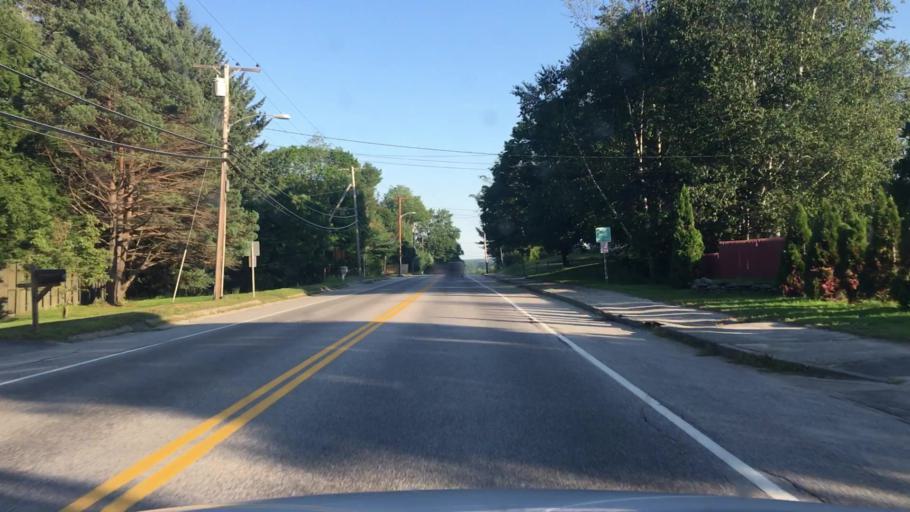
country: US
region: Maine
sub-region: Androscoggin County
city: Lisbon
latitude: 44.0178
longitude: -70.0920
